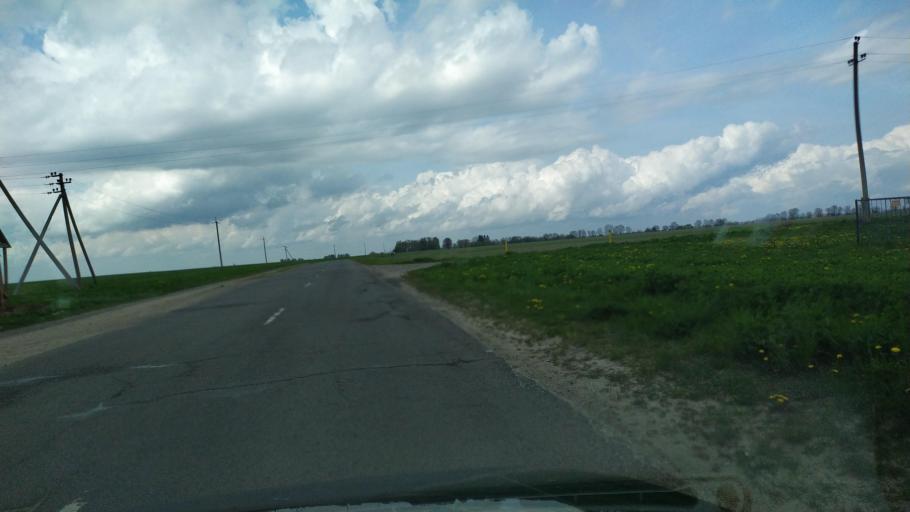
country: BY
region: Brest
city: Pruzhany
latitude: 52.6046
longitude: 24.4001
